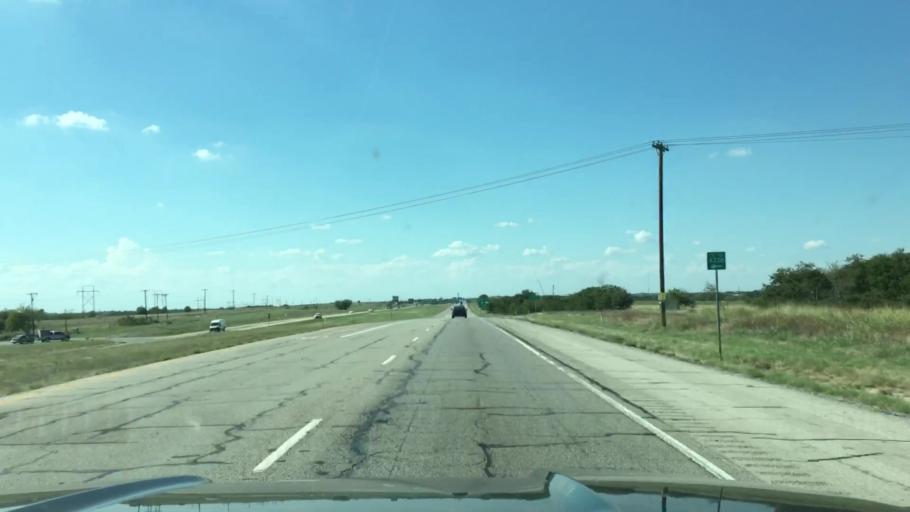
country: US
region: Texas
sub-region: Wise County
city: Decatur
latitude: 33.1792
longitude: -97.5464
